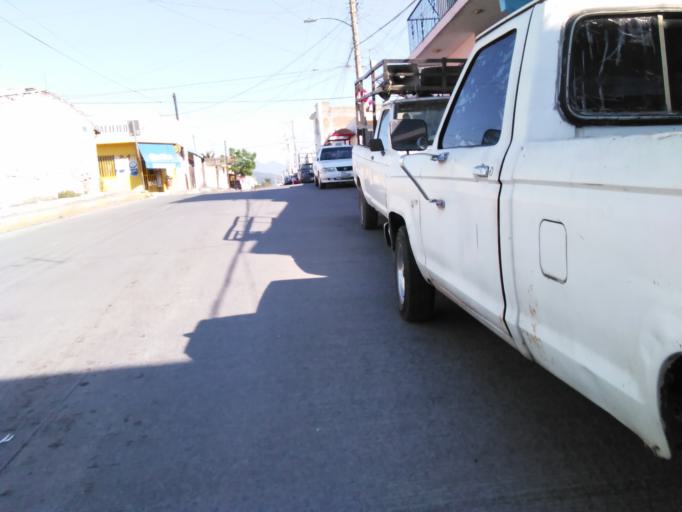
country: MX
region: Nayarit
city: Tepic
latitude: 21.5255
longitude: -104.8907
